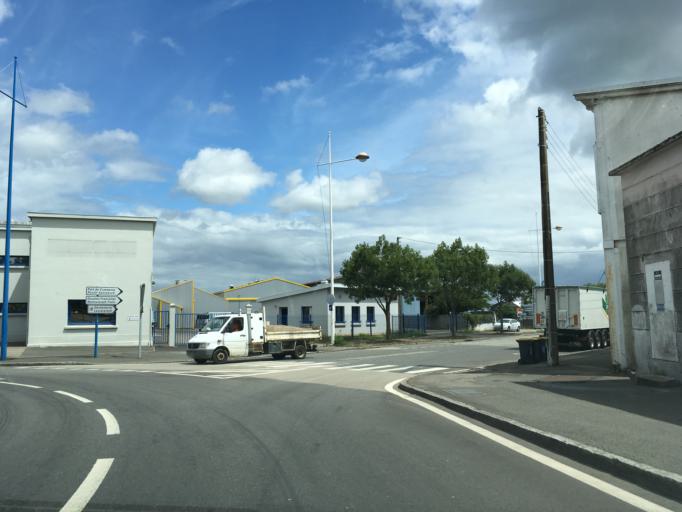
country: FR
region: Brittany
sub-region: Departement du Morbihan
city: Lorient
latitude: 47.7358
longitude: -3.3652
